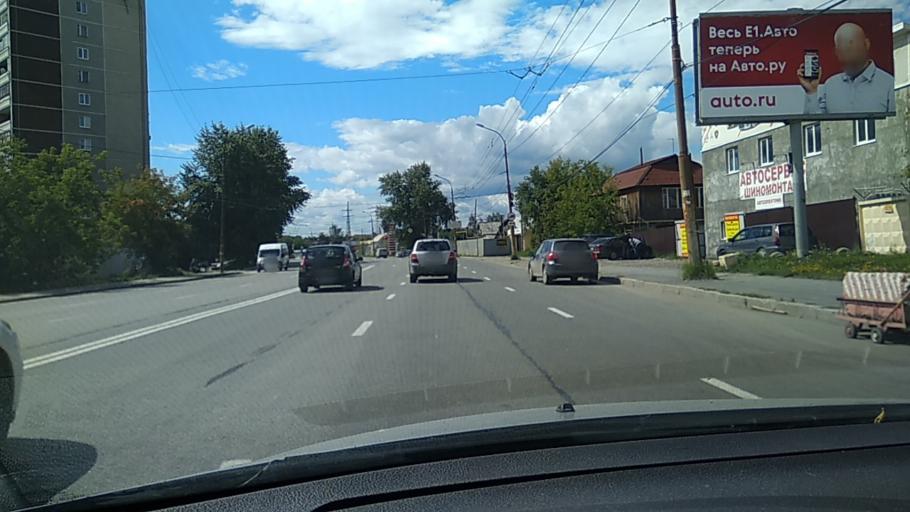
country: RU
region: Sverdlovsk
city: Verkhnyaya Pyshma
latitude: 56.9135
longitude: 60.6024
